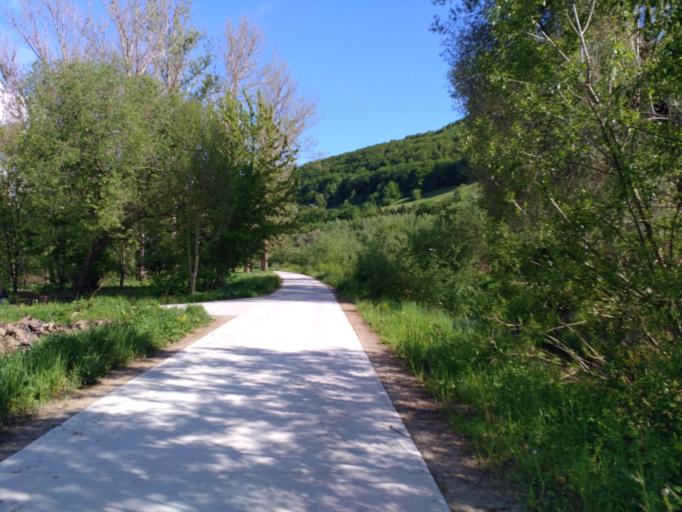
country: PL
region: Lesser Poland Voivodeship
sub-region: Powiat nowosadecki
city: Lacko
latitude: 49.5508
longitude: 20.4392
